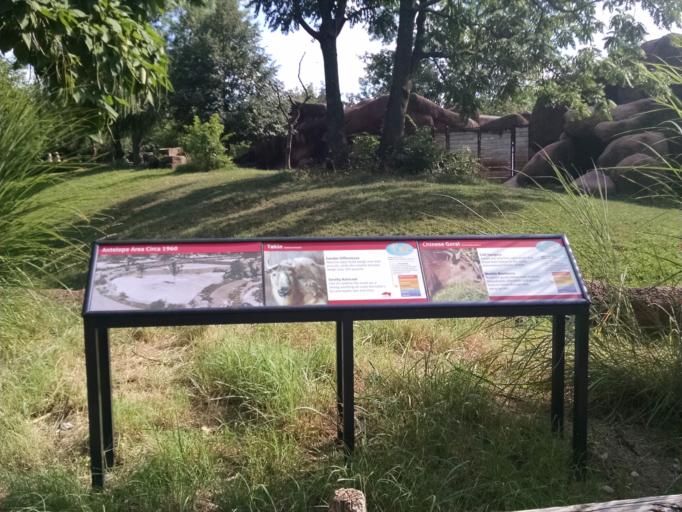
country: US
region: Missouri
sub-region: Saint Louis County
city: University City
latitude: 38.6343
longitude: -90.2864
